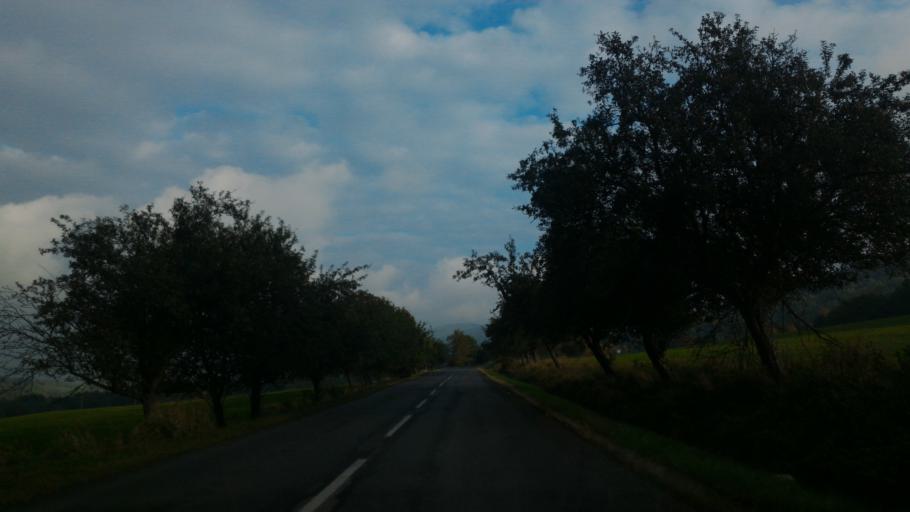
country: CZ
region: Ustecky
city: Dolni Podluzi
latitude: 50.8781
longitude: 14.5586
